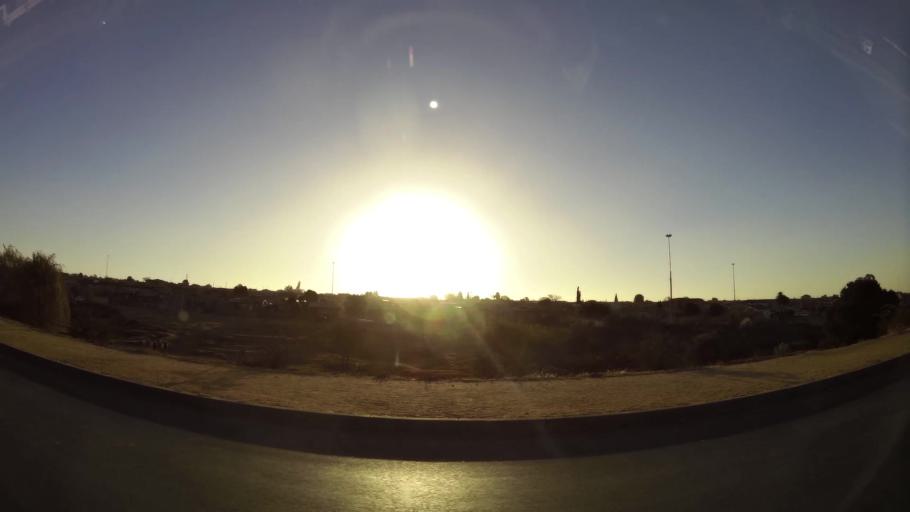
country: ZA
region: Gauteng
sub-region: Ekurhuleni Metropolitan Municipality
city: Tembisa
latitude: -26.0229
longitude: 28.1977
